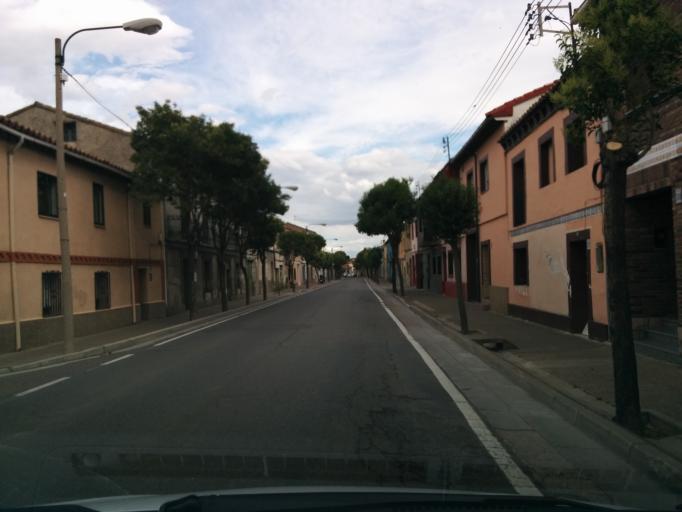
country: ES
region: Aragon
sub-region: Provincia de Zaragoza
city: Zaragoza
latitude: 41.6518
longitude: -0.8284
